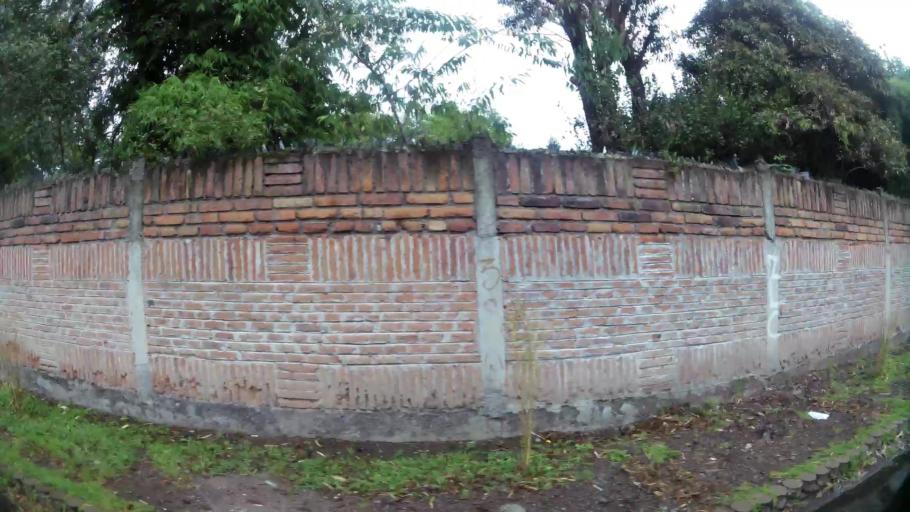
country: EC
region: Pichincha
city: Sangolqui
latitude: -0.2870
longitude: -78.4557
